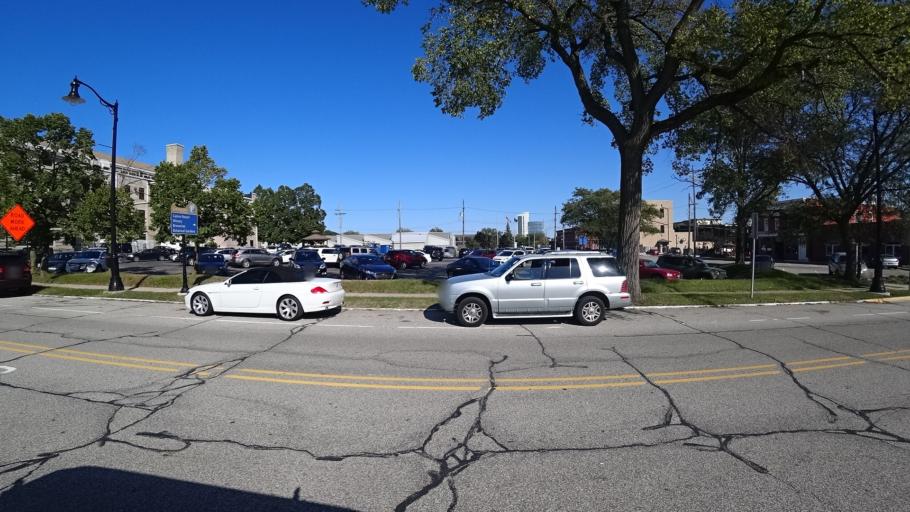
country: US
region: Indiana
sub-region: LaPorte County
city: Michigan City
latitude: 41.7183
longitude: -86.9040
